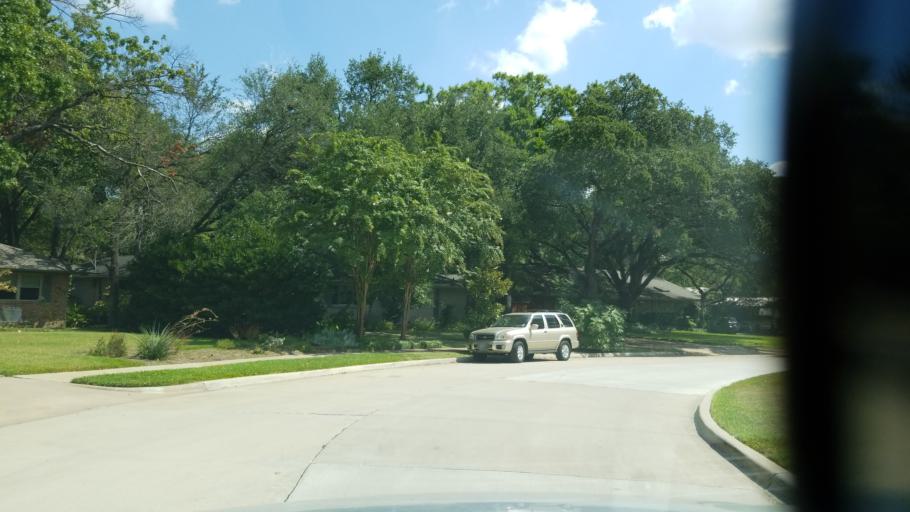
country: US
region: Texas
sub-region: Dallas County
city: Richardson
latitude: 32.9602
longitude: -96.7575
